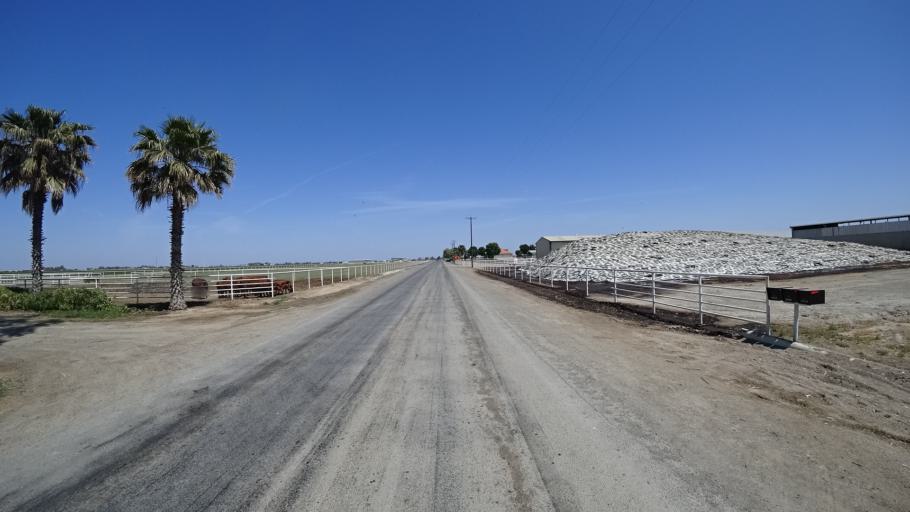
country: US
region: California
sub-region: Kings County
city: Stratford
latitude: 36.2080
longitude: -119.7623
